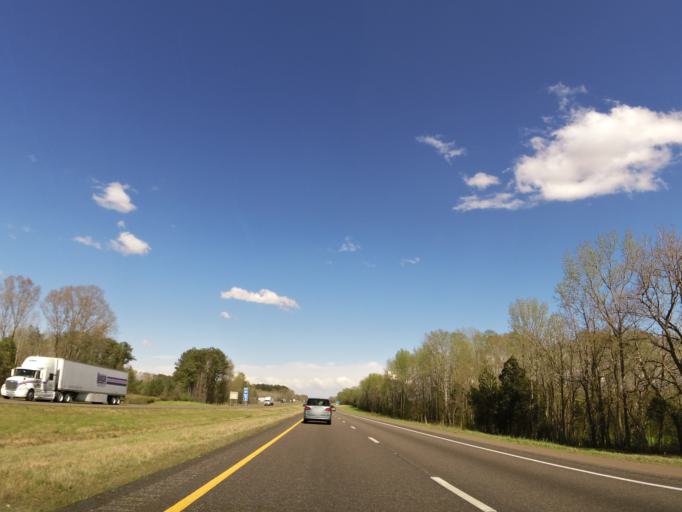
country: US
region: Tennessee
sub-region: Henderson County
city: Lexington
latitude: 35.7583
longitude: -88.4962
